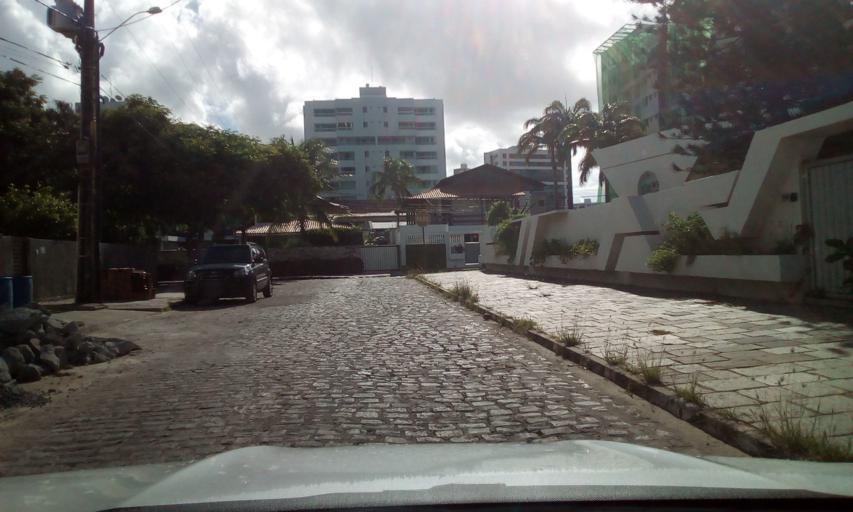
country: BR
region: Paraiba
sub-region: Joao Pessoa
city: Joao Pessoa
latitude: -7.0789
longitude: -34.8322
